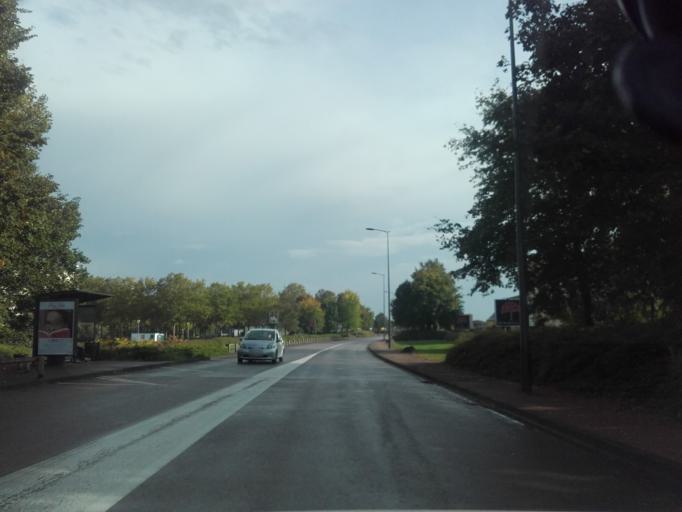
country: FR
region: Bourgogne
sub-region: Departement de la Cote-d'Or
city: Beaune
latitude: 47.0126
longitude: 4.8431
